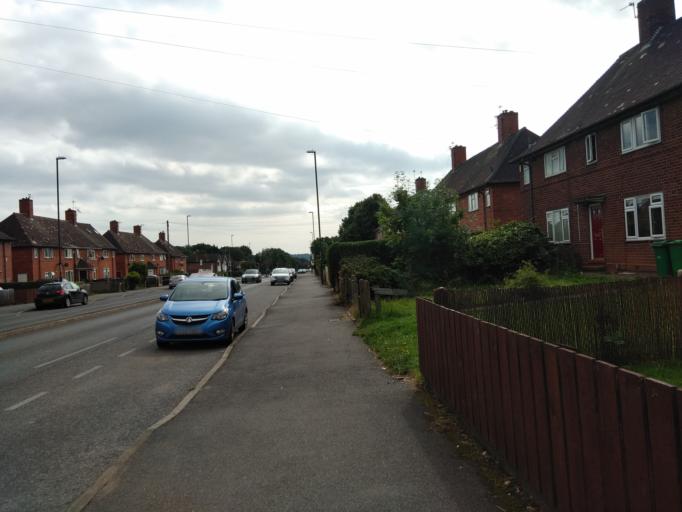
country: GB
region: England
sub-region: Nottinghamshire
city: Kimberley
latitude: 52.9695
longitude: -1.2125
